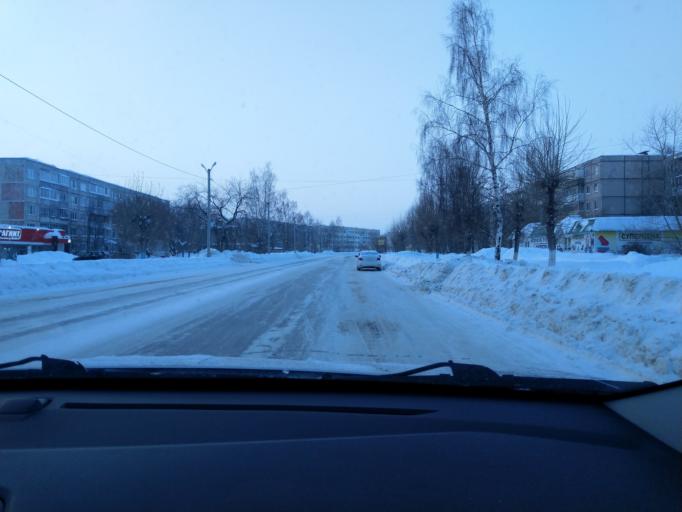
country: RU
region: Perm
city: Dobryanka
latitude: 58.4631
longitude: 56.3994
